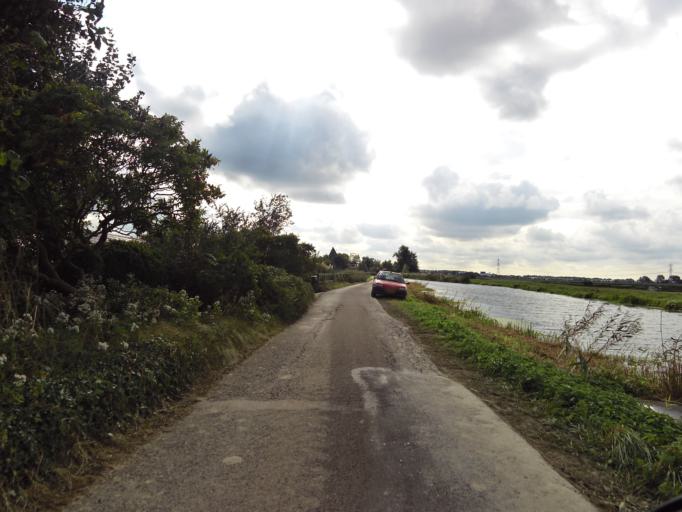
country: NL
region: South Holland
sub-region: Gemeente Rijnwoude
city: Benthuizen
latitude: 52.0445
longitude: 4.5621
